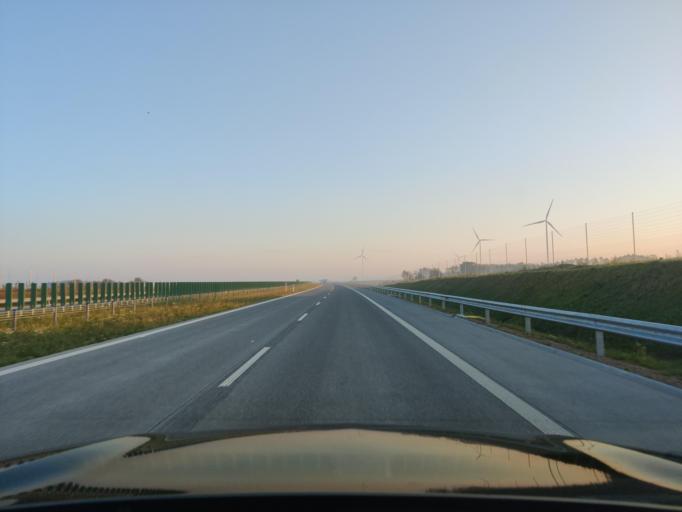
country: PL
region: Masovian Voivodeship
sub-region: Powiat mlawski
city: Wisniewo
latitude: 53.0390
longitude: 20.3563
